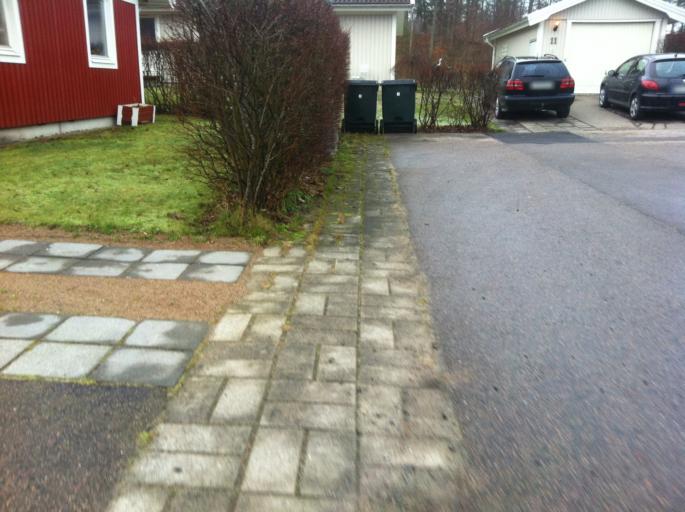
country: SE
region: Skane
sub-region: Perstorps Kommun
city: Perstorp
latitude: 56.1463
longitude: 13.3781
